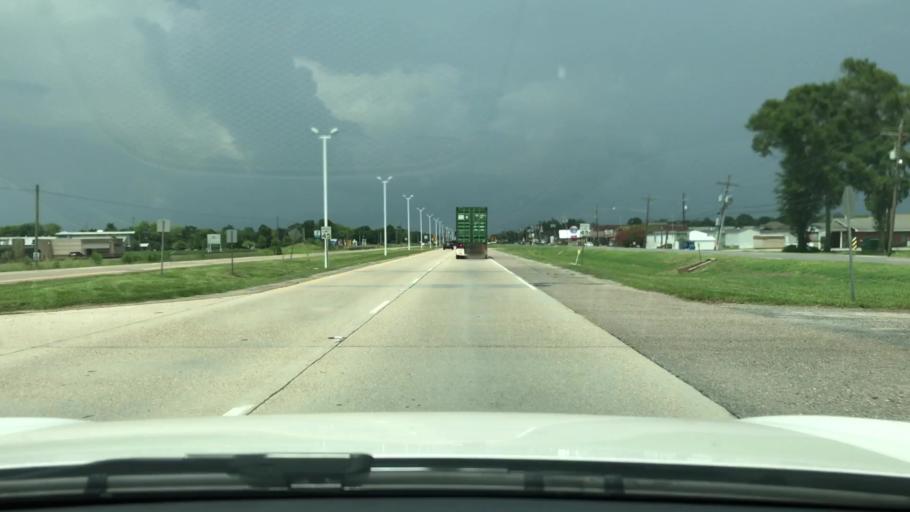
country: US
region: Louisiana
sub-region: West Baton Rouge Parish
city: Addis
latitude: 30.3706
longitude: -91.2565
